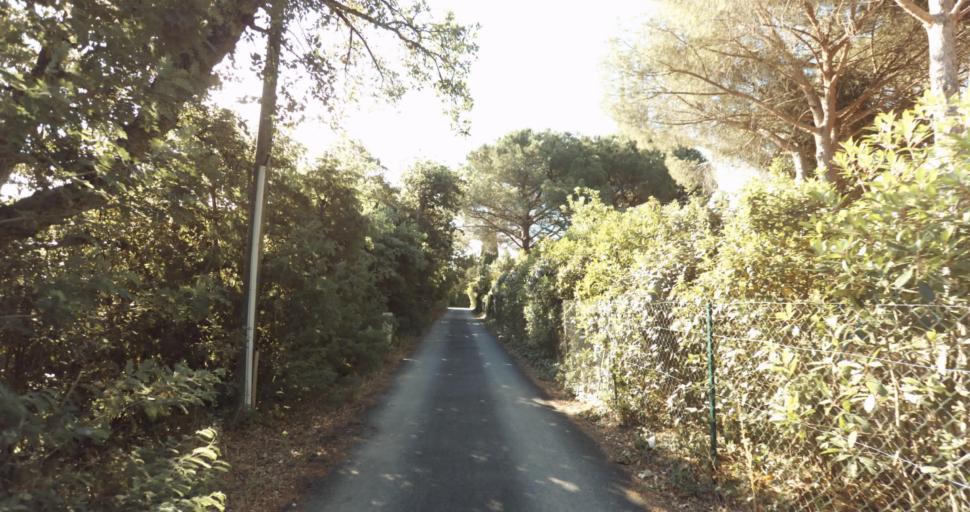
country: FR
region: Provence-Alpes-Cote d'Azur
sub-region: Departement du Var
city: Saint-Tropez
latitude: 43.2574
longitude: 6.6307
